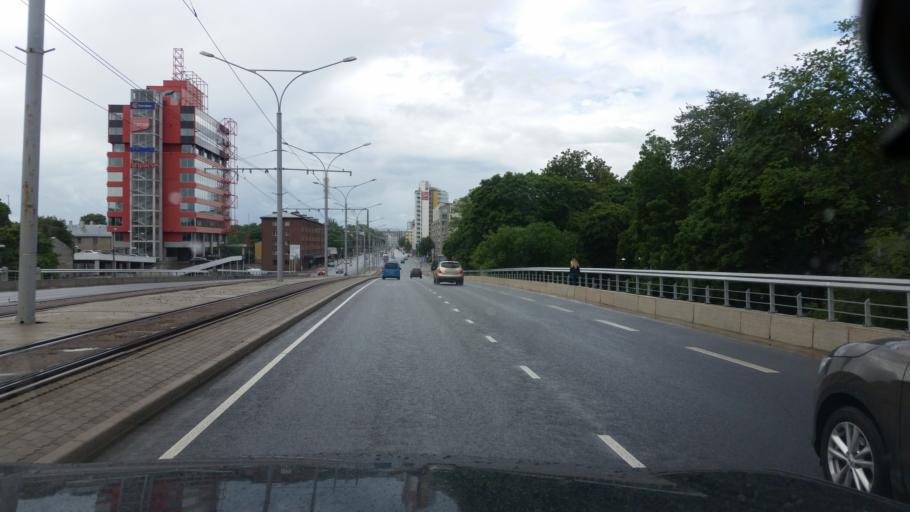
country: EE
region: Harju
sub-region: Tallinna linn
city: Tallinn
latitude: 59.4188
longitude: 24.7412
